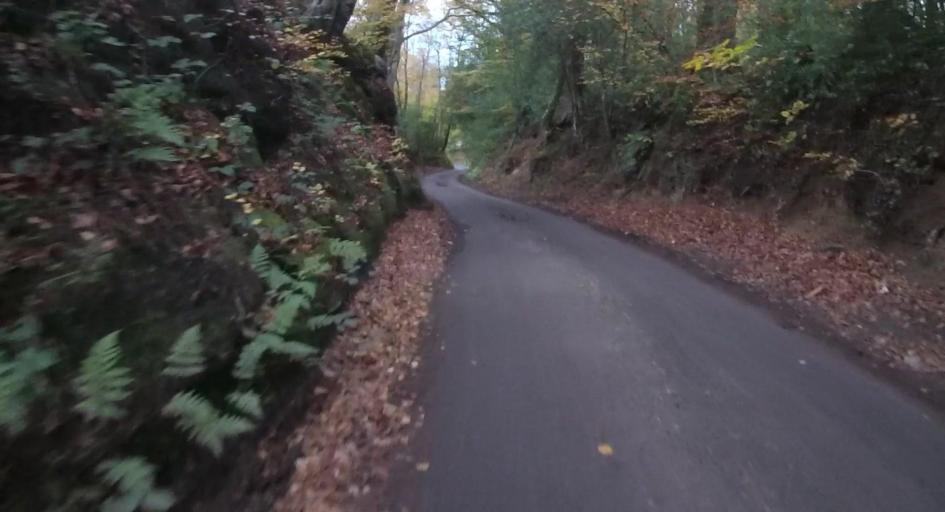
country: GB
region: England
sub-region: Surrey
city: Churt
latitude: 51.1320
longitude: -0.8112
